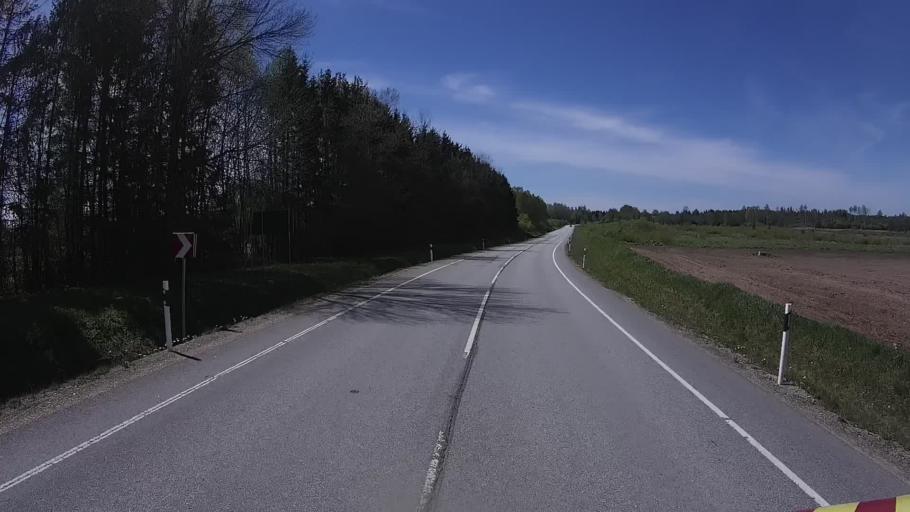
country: EE
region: Vorumaa
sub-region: Voru linn
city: Voru
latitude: 57.8906
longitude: 27.1765
